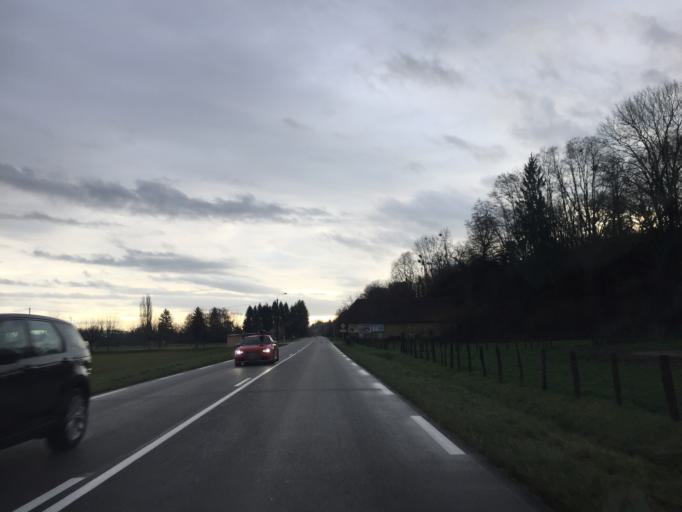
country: FR
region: Franche-Comte
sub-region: Departement du Jura
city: Mont-sous-Vaudrey
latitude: 46.9978
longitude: 5.5394
